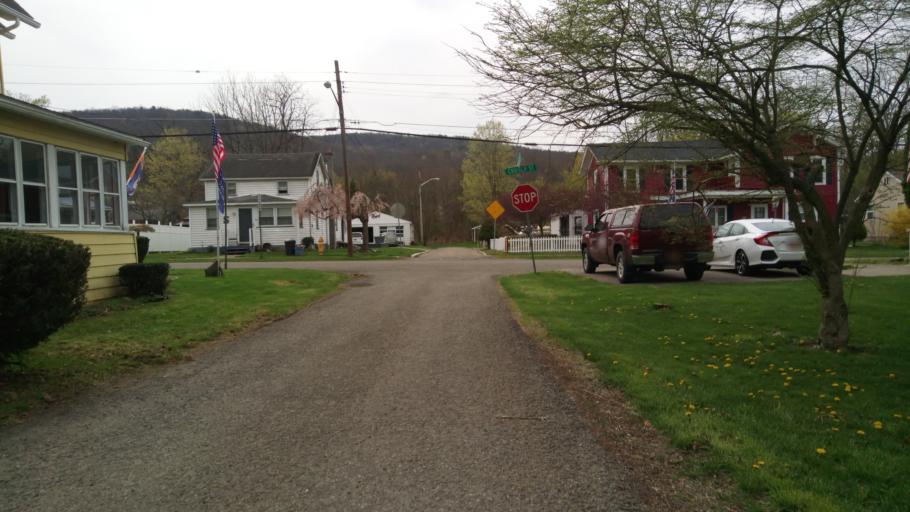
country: US
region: New York
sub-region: Chemung County
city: Southport
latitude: 42.0147
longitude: -76.7289
